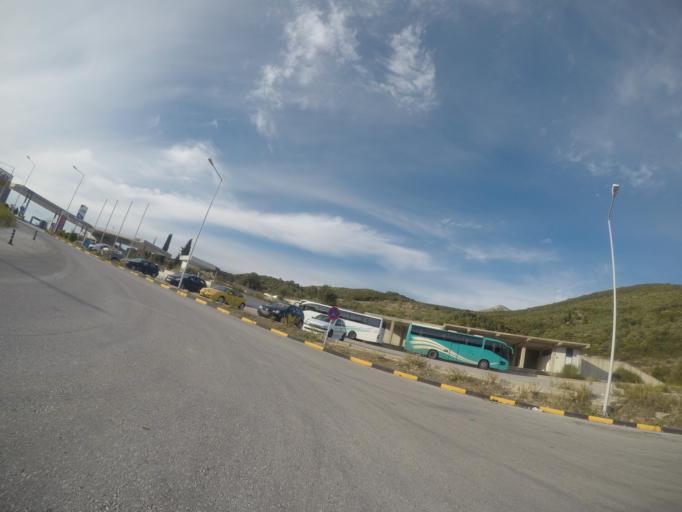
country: GR
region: Epirus
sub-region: Nomos Thesprotias
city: Plataria
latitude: 39.4517
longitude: 20.3594
